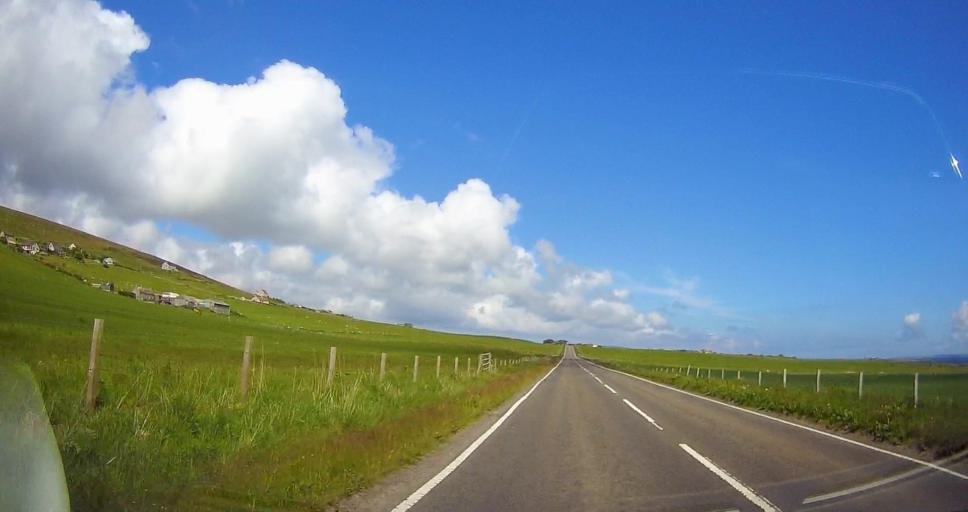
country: GB
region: Scotland
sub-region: Orkney Islands
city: Orkney
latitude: 59.0148
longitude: -3.1077
